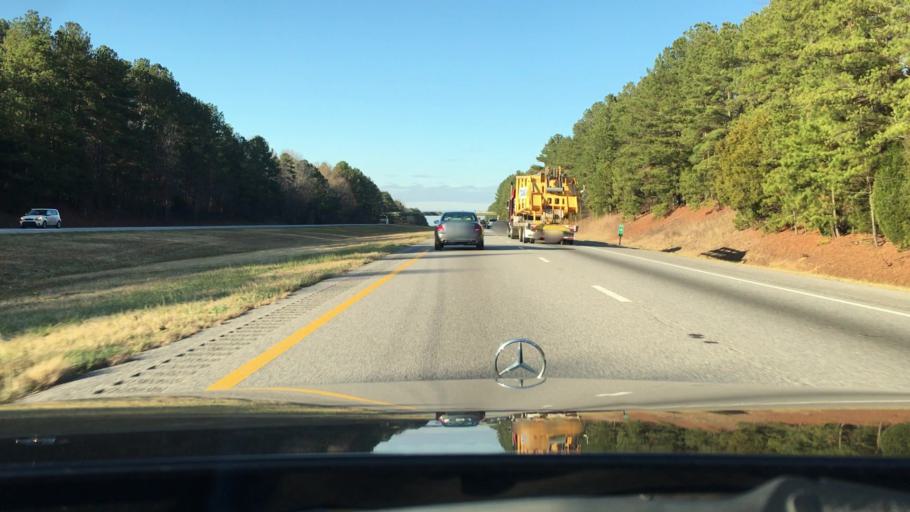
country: US
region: South Carolina
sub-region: Chester County
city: Eureka Mill
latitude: 34.6922
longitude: -81.0295
